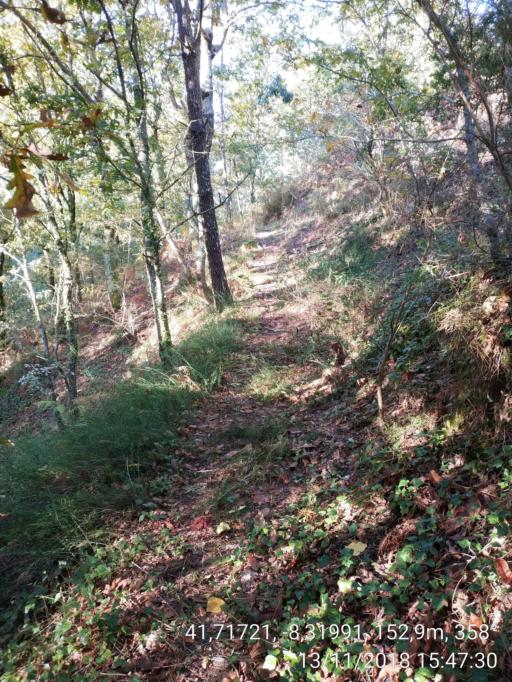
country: PT
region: Braga
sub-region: Terras de Bouro
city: Terras de Bouro
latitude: 41.7172
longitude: -8.3199
